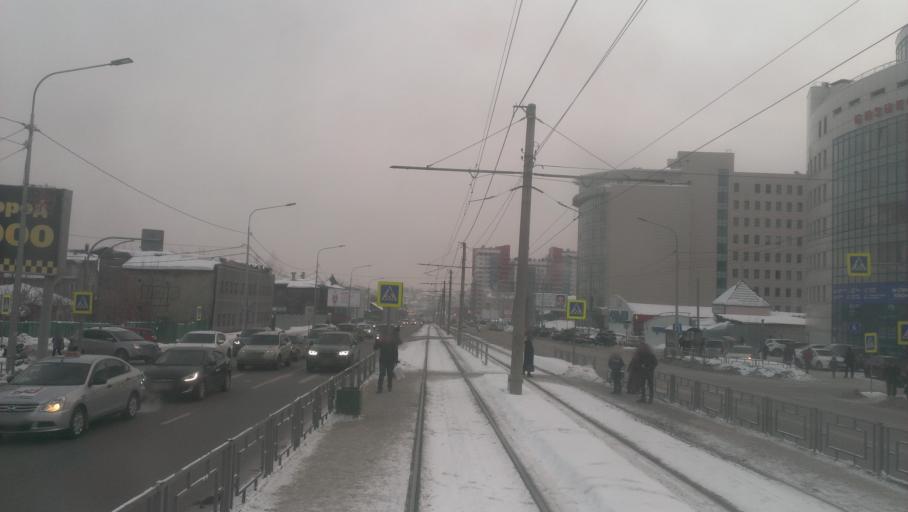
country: RU
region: Altai Krai
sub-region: Gorod Barnaulskiy
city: Barnaul
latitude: 53.3355
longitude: 83.7771
